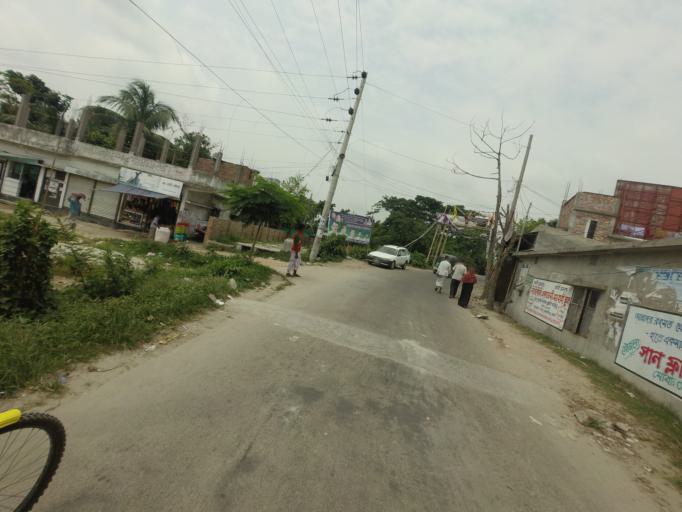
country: BD
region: Dhaka
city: Azimpur
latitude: 23.7300
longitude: 90.3496
